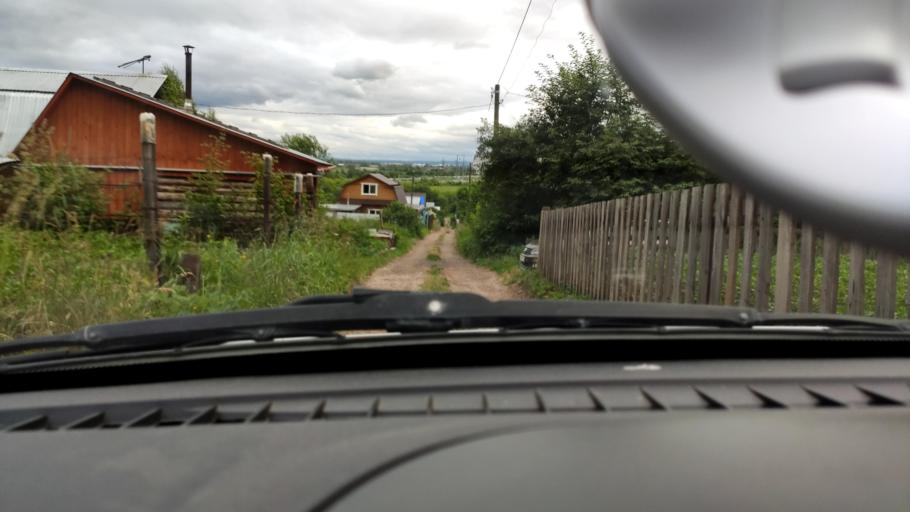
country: RU
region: Perm
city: Kondratovo
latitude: 57.9443
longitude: 56.1665
